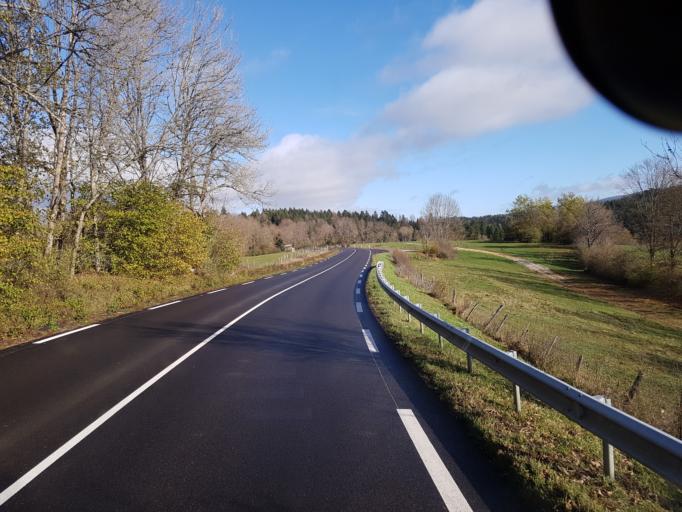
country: FR
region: Franche-Comte
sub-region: Departement du Jura
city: Morbier
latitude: 46.5871
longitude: 5.9534
